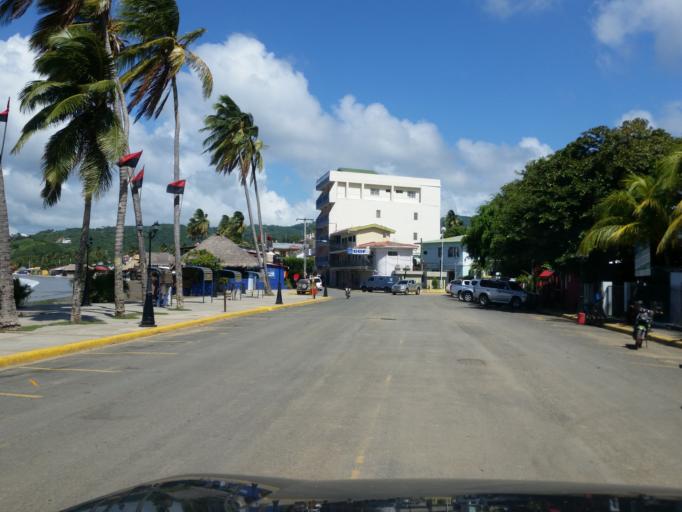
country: NI
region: Rivas
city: San Juan del Sur
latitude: 11.2513
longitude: -85.8727
